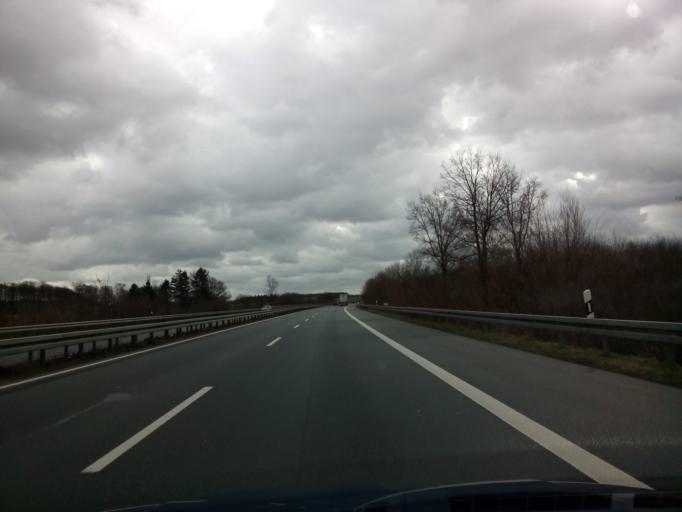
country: DE
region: Lower Saxony
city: Wallenhorst
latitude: 52.3311
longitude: 8.0299
